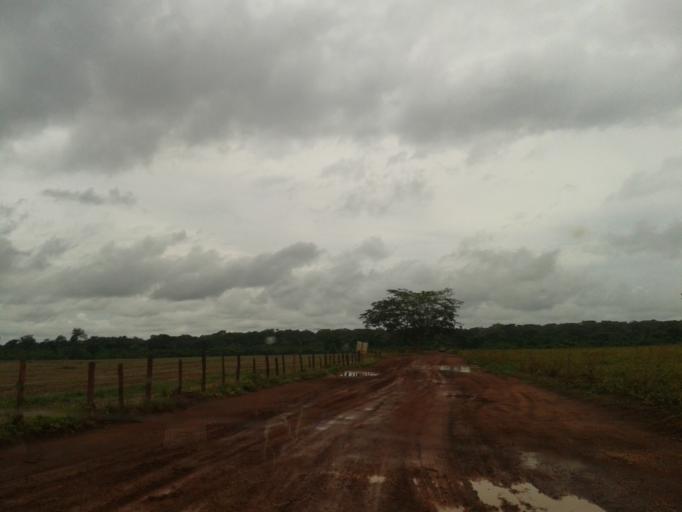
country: BR
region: Minas Gerais
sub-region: Santa Vitoria
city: Santa Vitoria
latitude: -18.7074
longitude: -49.9644
